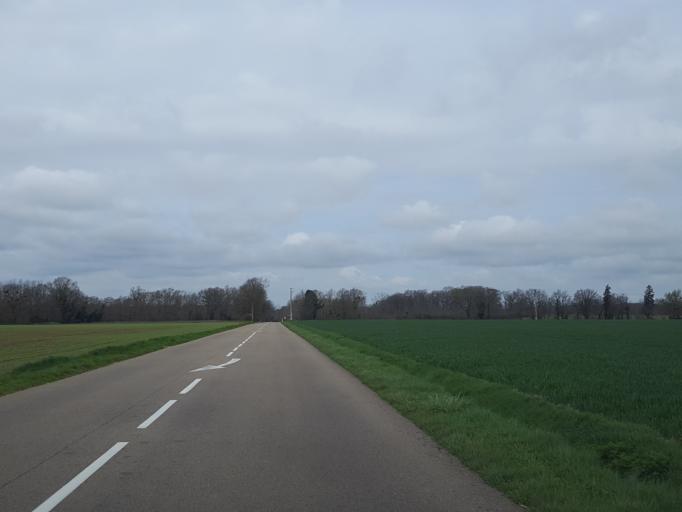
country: FR
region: Centre
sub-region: Departement du Loiret
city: Sainte-Genevieve-des-Bois
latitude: 47.8210
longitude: 2.8278
